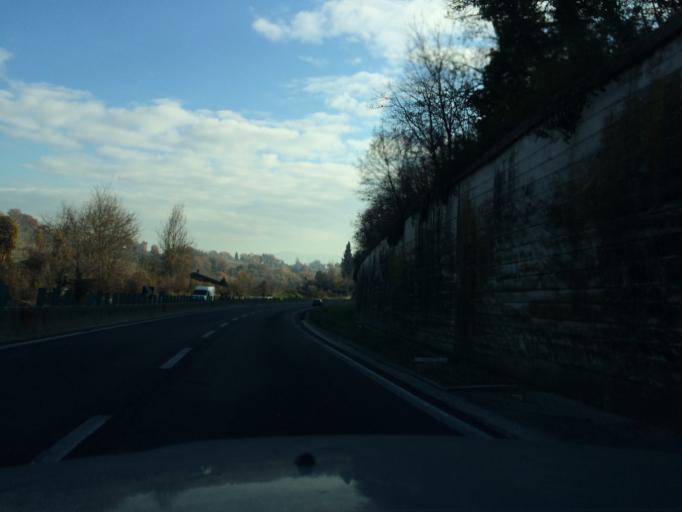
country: IT
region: Umbria
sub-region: Provincia di Terni
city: San Gemini
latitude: 42.6042
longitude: 12.5610
